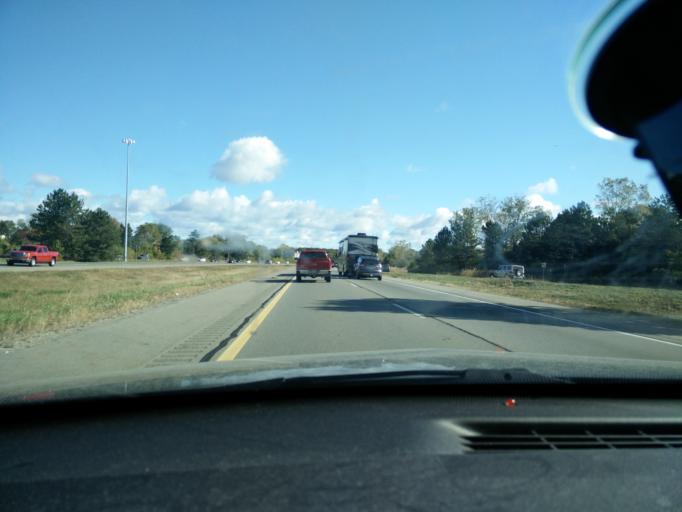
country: US
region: Michigan
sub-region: Oakland County
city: Farmington Hills
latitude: 42.4882
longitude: -83.4252
